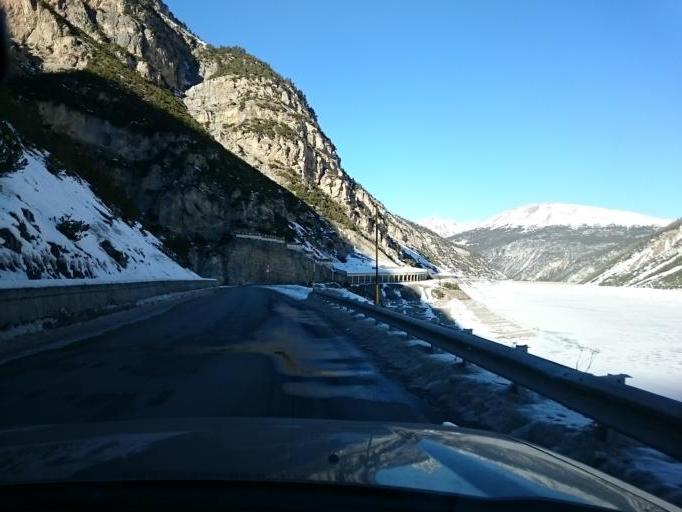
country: IT
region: Lombardy
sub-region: Provincia di Sondrio
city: Livigno
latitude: 46.6034
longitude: 10.1747
